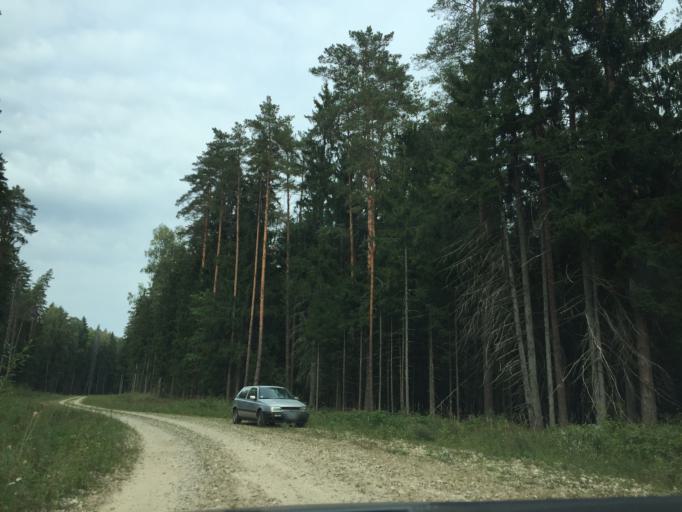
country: LV
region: Baldone
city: Baldone
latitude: 56.7504
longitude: 24.4667
